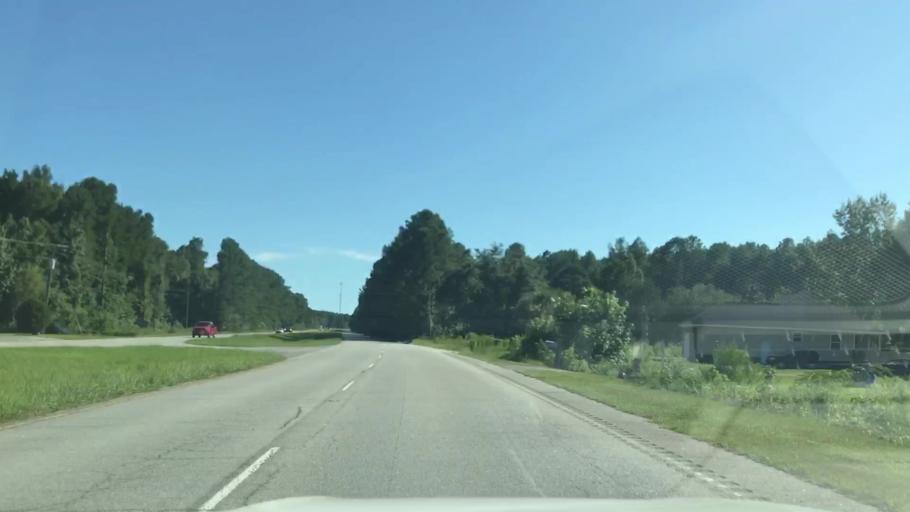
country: US
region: South Carolina
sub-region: Charleston County
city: Awendaw
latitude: 33.0018
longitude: -79.6437
